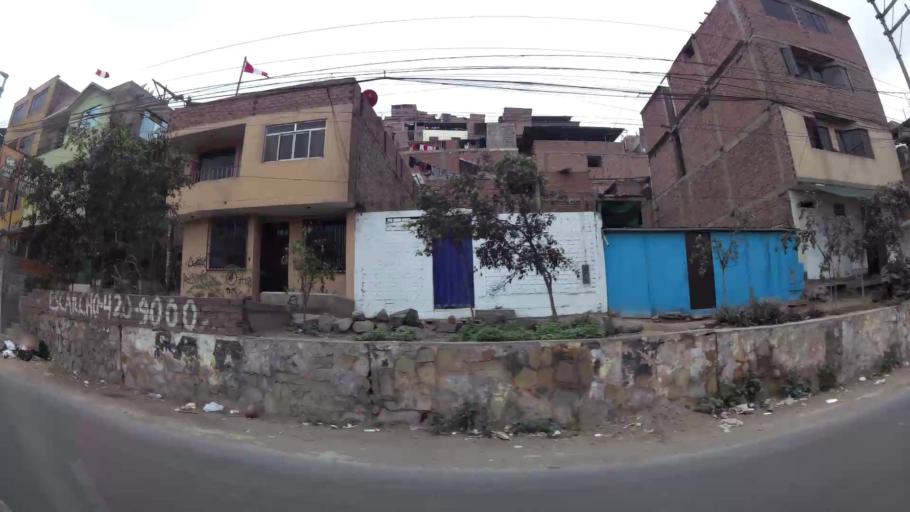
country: PE
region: Lima
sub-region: Lima
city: Surco
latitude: -12.1385
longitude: -76.9749
